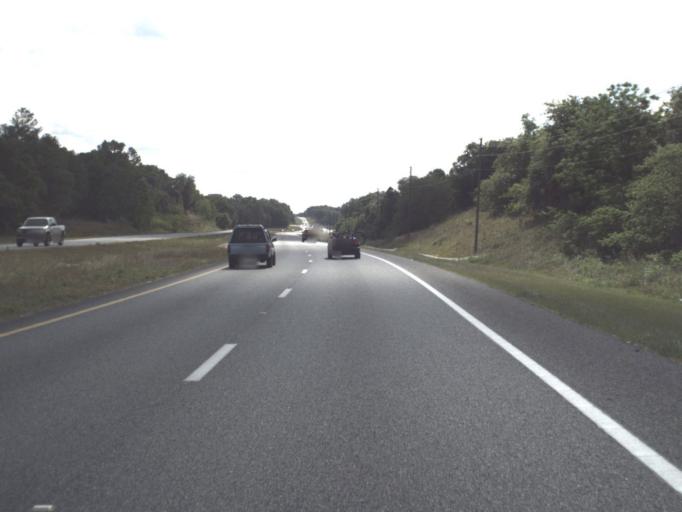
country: US
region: Florida
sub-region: Marion County
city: Ocala
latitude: 29.2599
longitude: -82.1635
